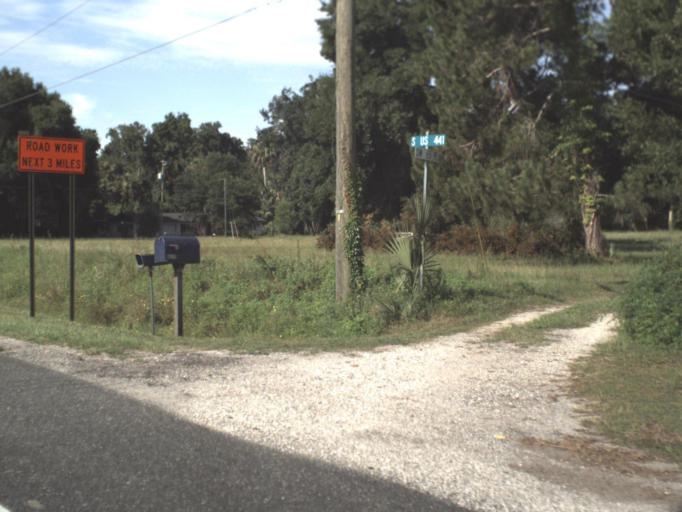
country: US
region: Florida
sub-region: Alachua County
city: Gainesville
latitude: 29.5924
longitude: -82.3392
